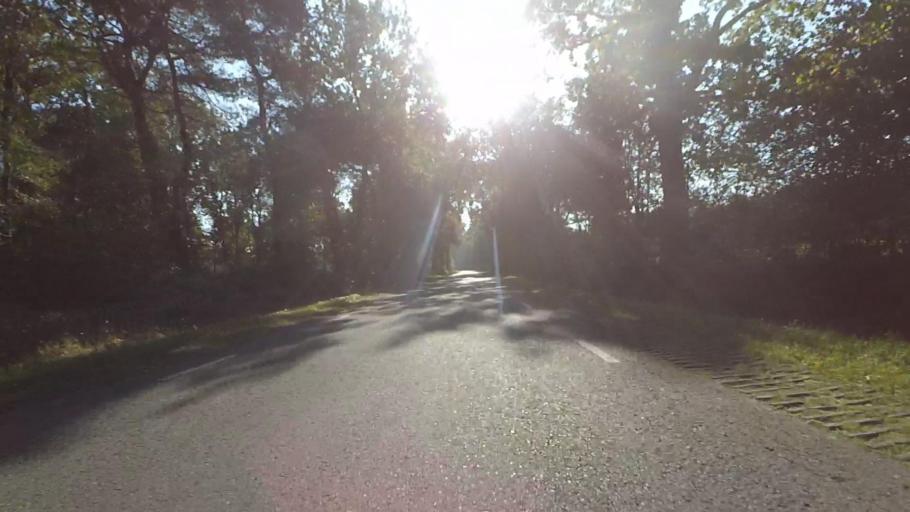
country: NL
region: Gelderland
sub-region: Gemeente Putten
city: Putten
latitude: 52.2431
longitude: 5.5535
